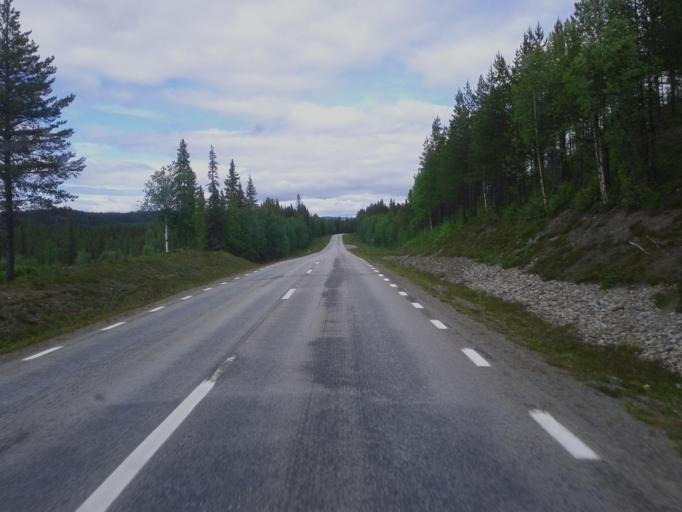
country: SE
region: Vaesterbotten
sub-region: Storumans Kommun
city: Fristad
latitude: 65.3632
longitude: 16.5296
